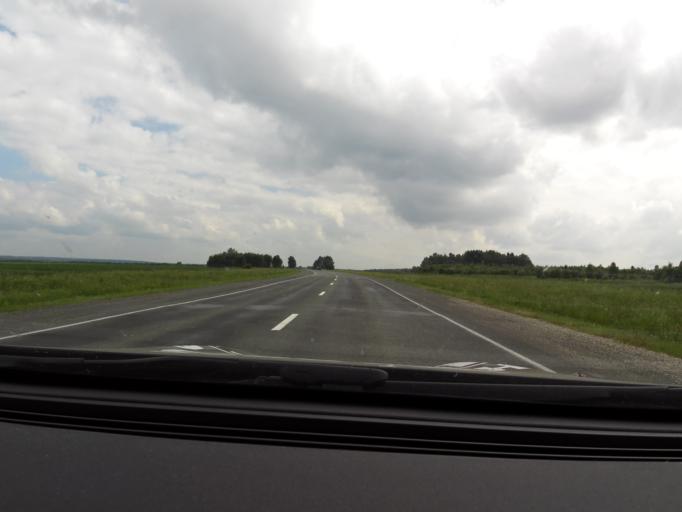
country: RU
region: Perm
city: Suksun
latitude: 56.9399
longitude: 57.5360
